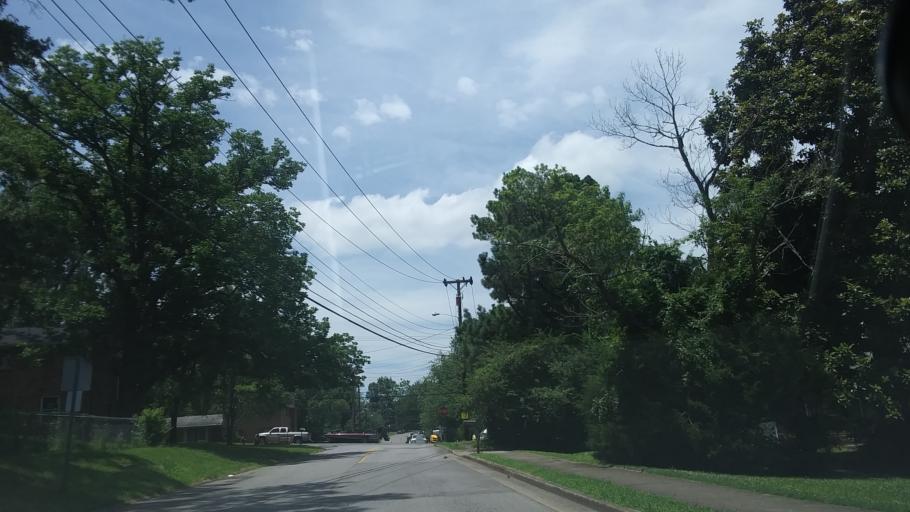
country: US
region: Tennessee
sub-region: Rutherford County
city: La Vergne
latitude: 36.0826
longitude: -86.6278
